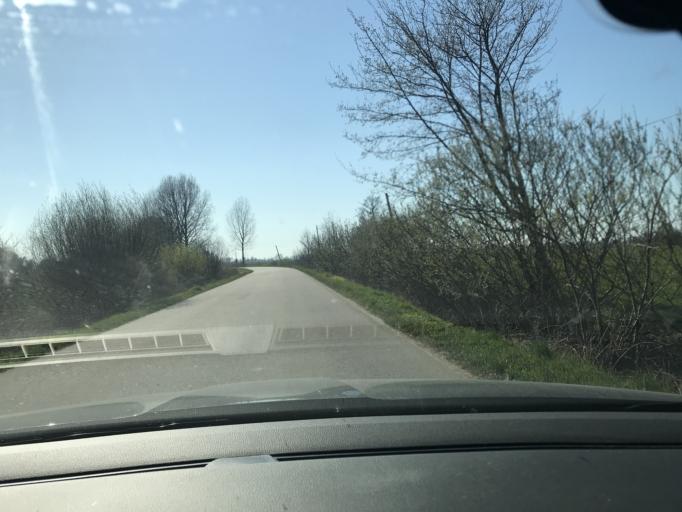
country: PL
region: Pomeranian Voivodeship
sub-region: Powiat nowodworski
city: Stegna
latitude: 54.2966
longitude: 19.1345
